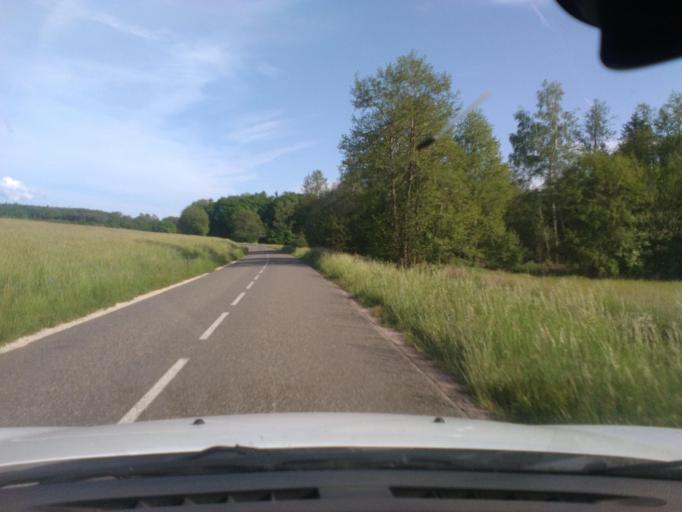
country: FR
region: Lorraine
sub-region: Departement des Vosges
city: Jeanmenil
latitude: 48.2910
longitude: 6.6923
